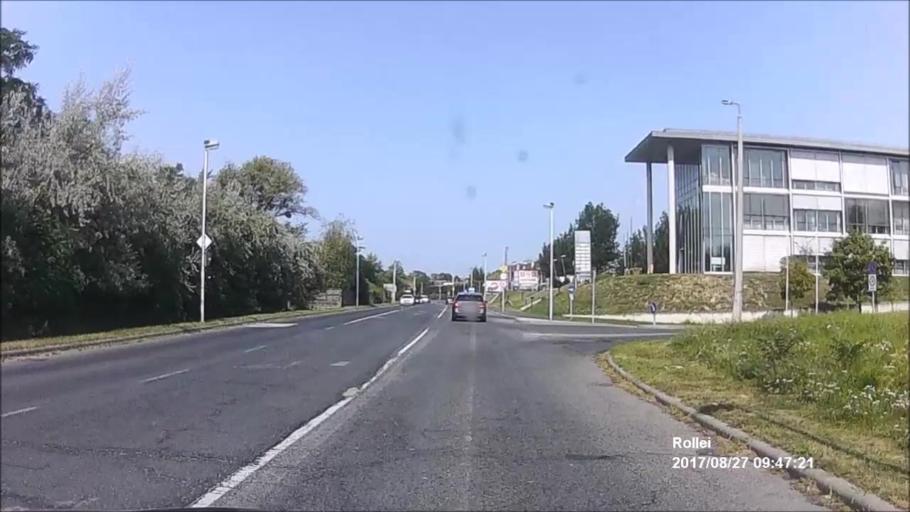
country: HU
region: Gyor-Moson-Sopron
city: Sopron
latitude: 47.6866
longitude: 16.6069
